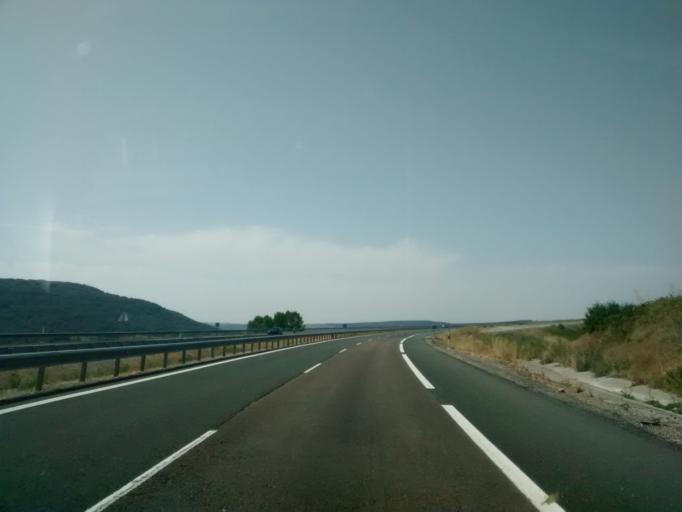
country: ES
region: Castille and Leon
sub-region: Provincia de Palencia
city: Aguilar de Campoo
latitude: 42.8196
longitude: -4.2063
